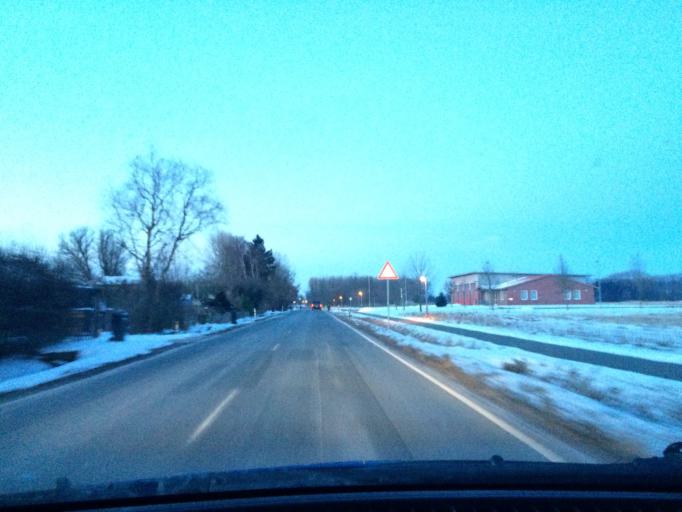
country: DE
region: Lower Saxony
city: Marschacht
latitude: 53.4140
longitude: 10.3653
